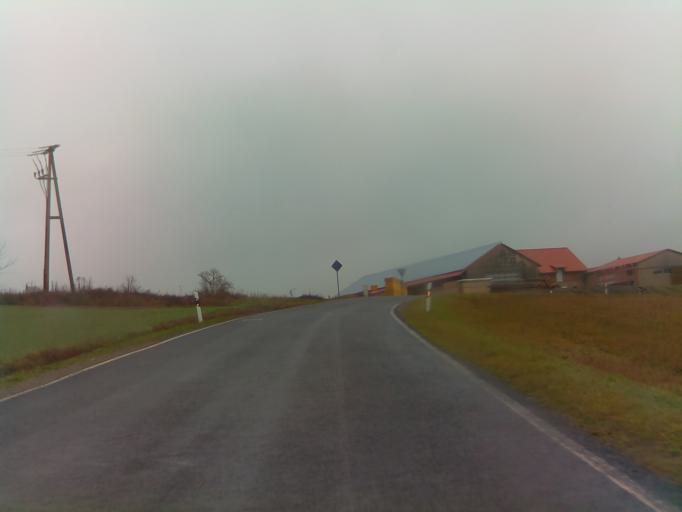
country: DE
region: Thuringia
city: Dingsleben
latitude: 50.4302
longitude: 10.6016
